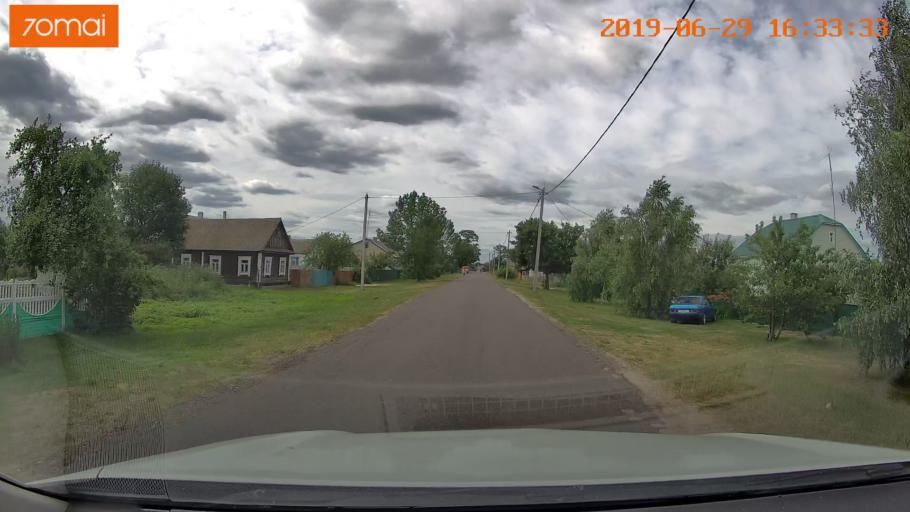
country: BY
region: Brest
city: Luninyets
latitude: 52.2028
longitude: 27.0122
